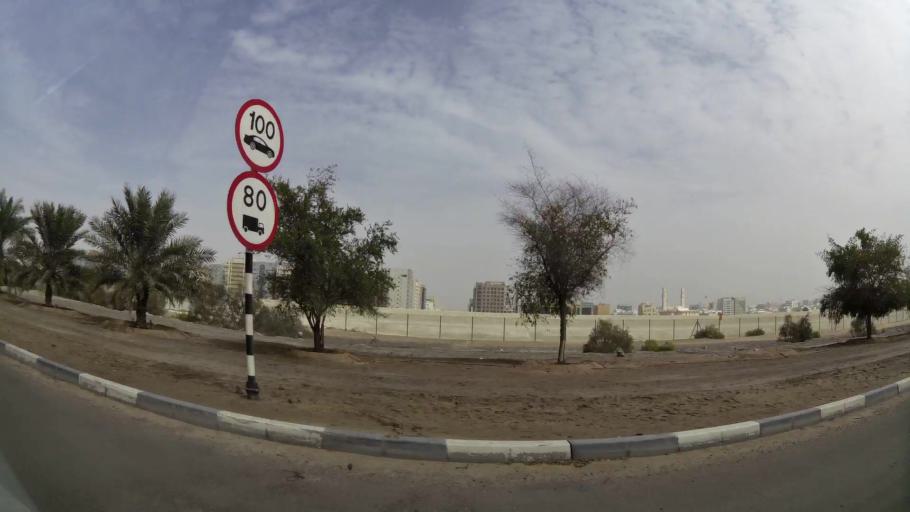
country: AE
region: Abu Dhabi
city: Abu Dhabi
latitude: 24.3332
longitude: 54.5271
